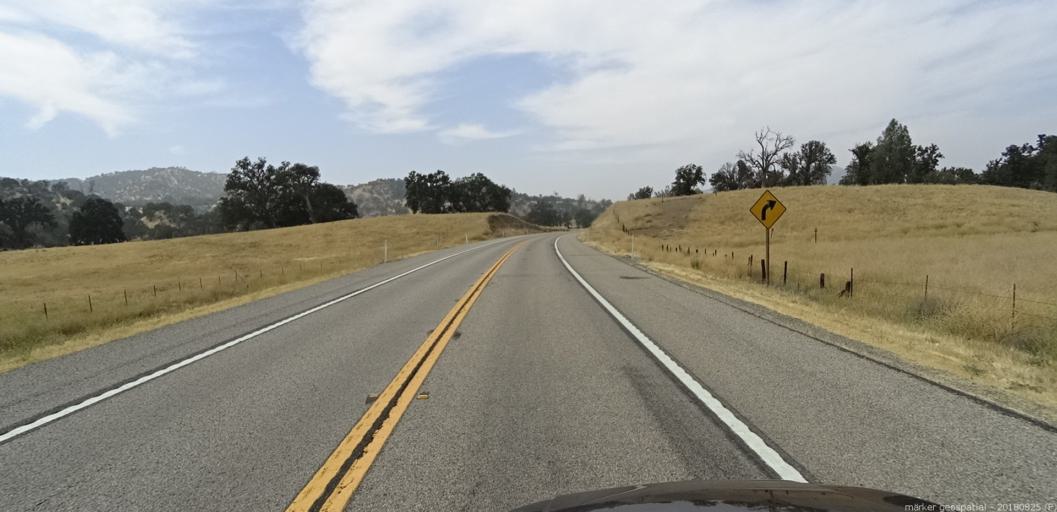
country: US
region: California
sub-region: Fresno County
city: Coalinga
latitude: 36.1853
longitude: -120.7031
